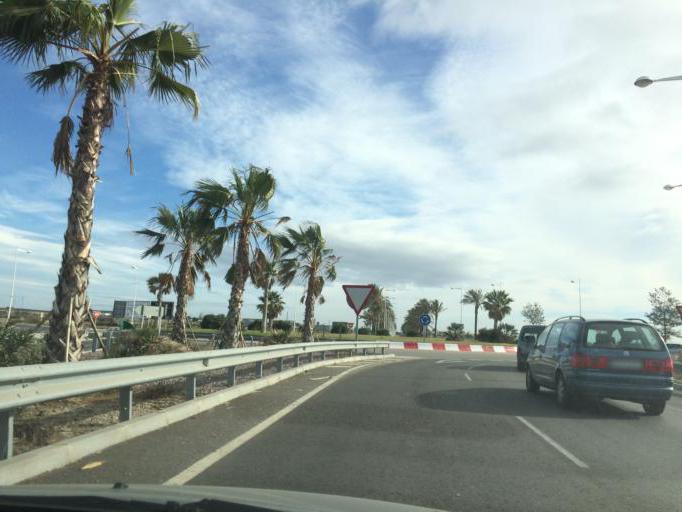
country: ES
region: Andalusia
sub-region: Provincia de Almeria
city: Retamar
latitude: 36.8521
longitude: -2.3211
